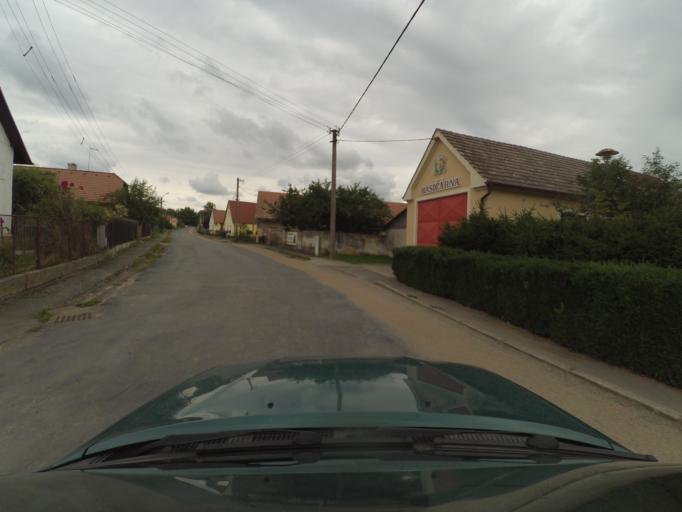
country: CZ
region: Plzensky
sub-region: Okres Rokycany
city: Brasy
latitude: 49.8693
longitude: 13.5125
